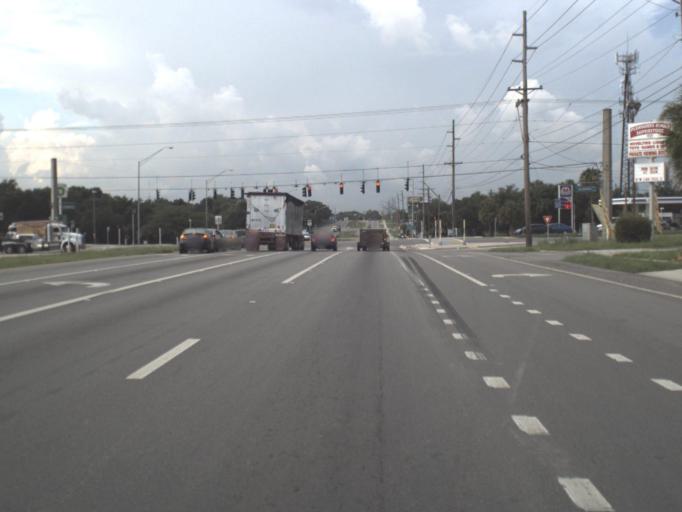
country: US
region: Florida
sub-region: Hillsborough County
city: East Lake-Orient Park
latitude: 27.9972
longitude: -82.3936
